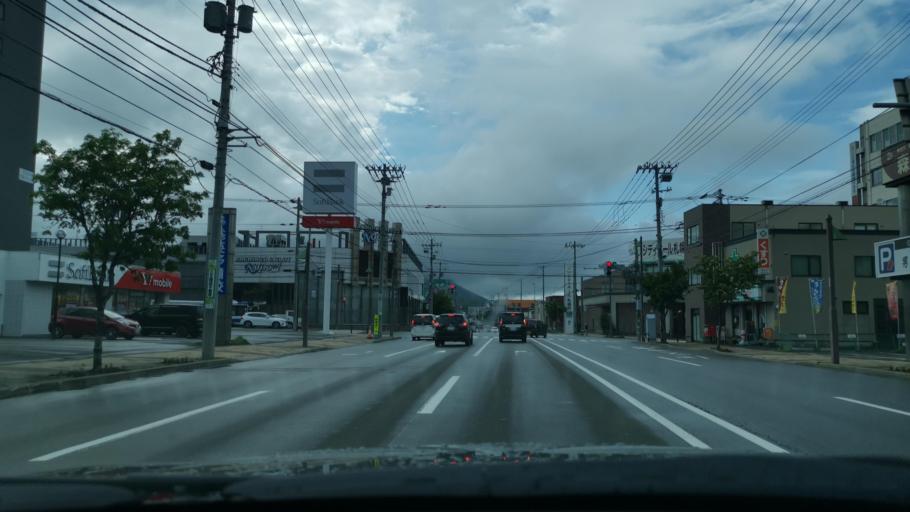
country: JP
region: Hokkaido
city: Sapporo
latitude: 43.0743
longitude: 141.2835
